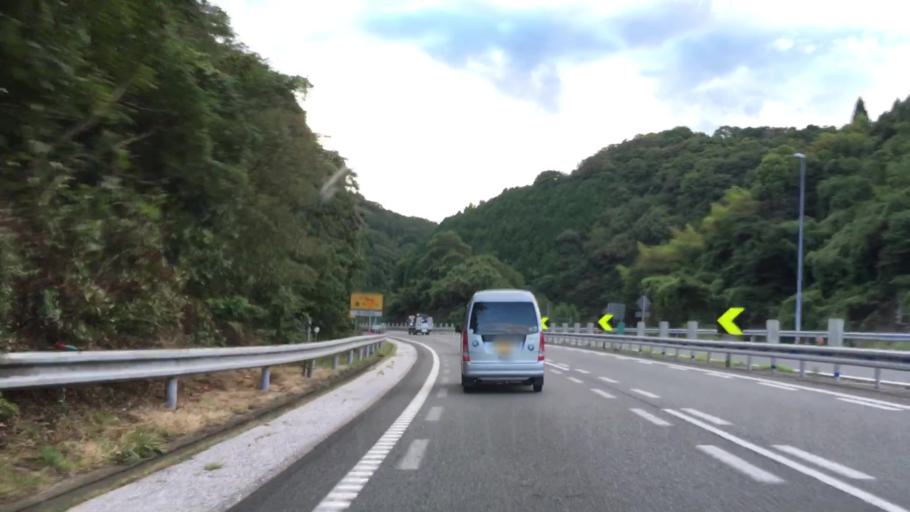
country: JP
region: Yamaguchi
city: Onoda
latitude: 34.1189
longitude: 131.2026
